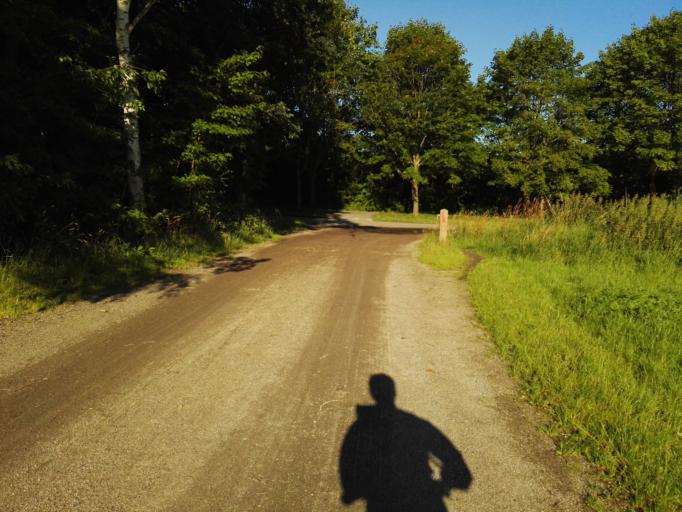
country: DK
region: Capital Region
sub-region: Ballerup Kommune
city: Ballerup
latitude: 55.7172
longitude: 12.3756
